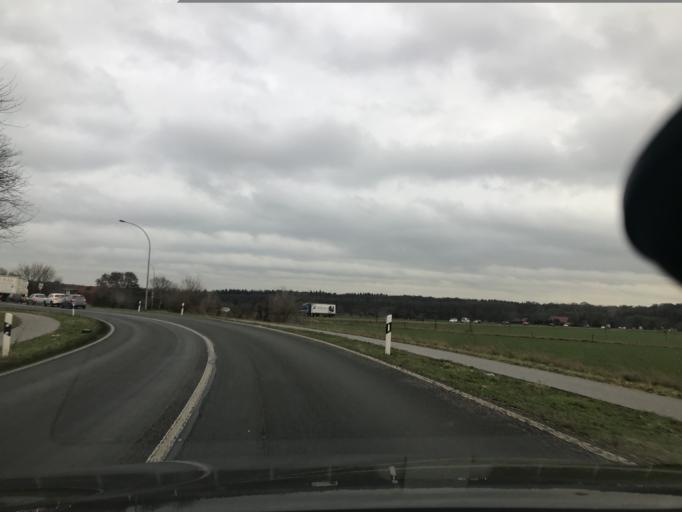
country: DE
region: North Rhine-Westphalia
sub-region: Regierungsbezirk Dusseldorf
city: Kleve
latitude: 51.7810
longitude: 6.1538
